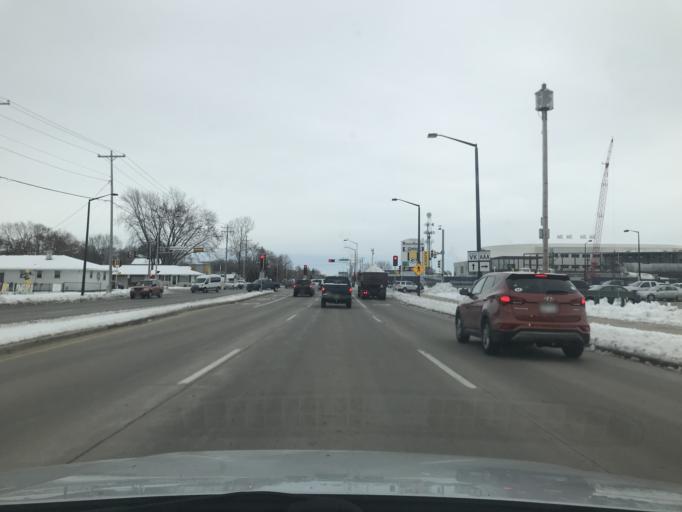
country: US
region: Wisconsin
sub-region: Brown County
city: Ashwaubenon
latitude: 44.5019
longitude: -88.0580
